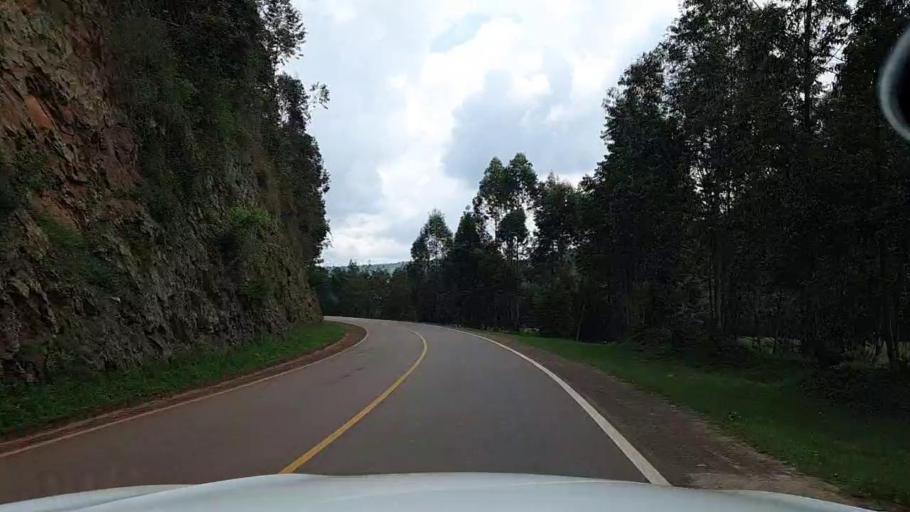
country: RW
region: Kigali
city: Kigali
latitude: -1.8180
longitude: 30.1166
